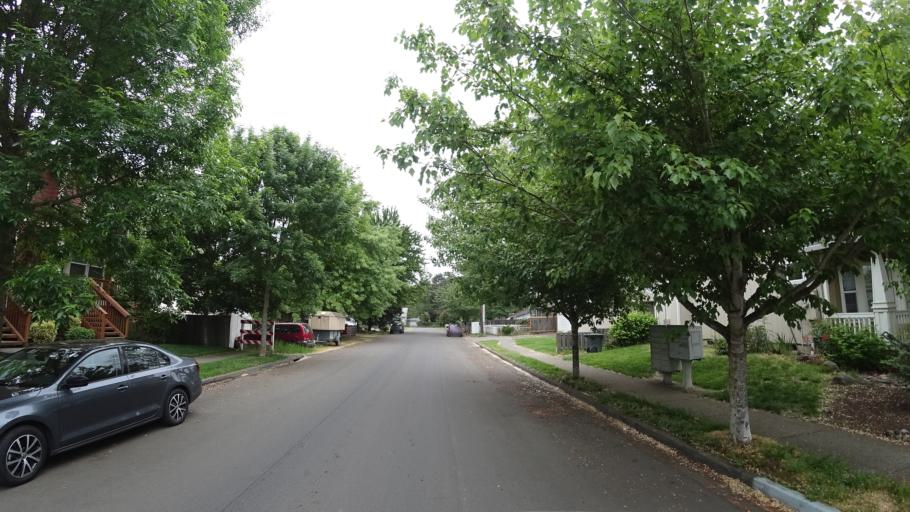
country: US
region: Oregon
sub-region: Washington County
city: Aloha
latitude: 45.4997
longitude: -122.9098
